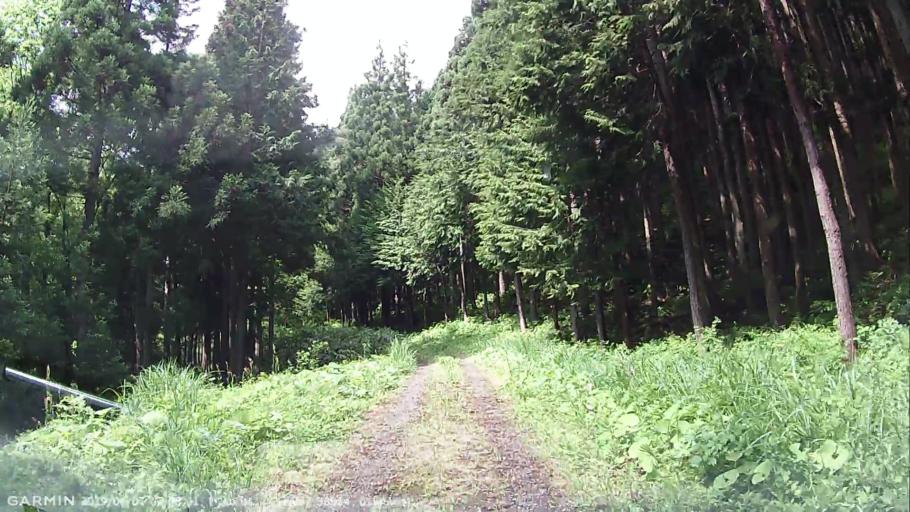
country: JP
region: Fukushima
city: Inawashiro
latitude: 37.3851
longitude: 140.0612
